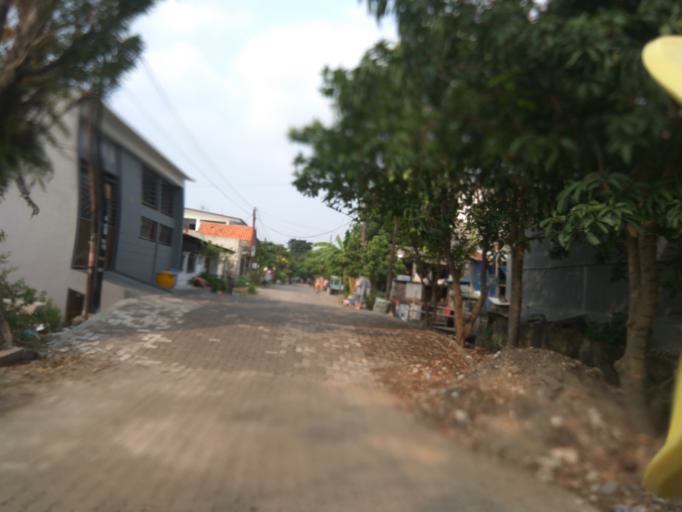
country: ID
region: Central Java
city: Semarang
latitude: -6.9751
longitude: 110.3914
